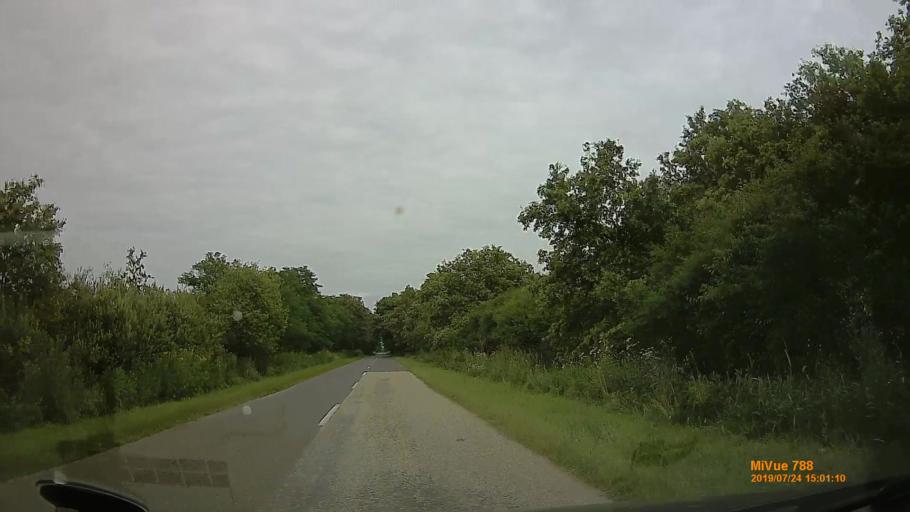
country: HU
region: Szabolcs-Szatmar-Bereg
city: Vasarosnameny
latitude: 48.2296
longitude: 22.3838
